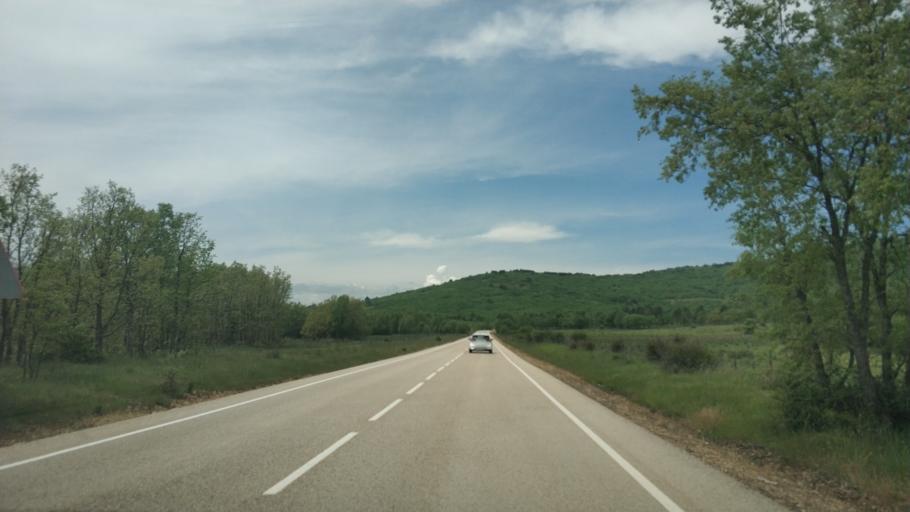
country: ES
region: Castille and Leon
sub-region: Provincia de Soria
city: Vinuesa
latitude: 41.8875
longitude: -2.6938
